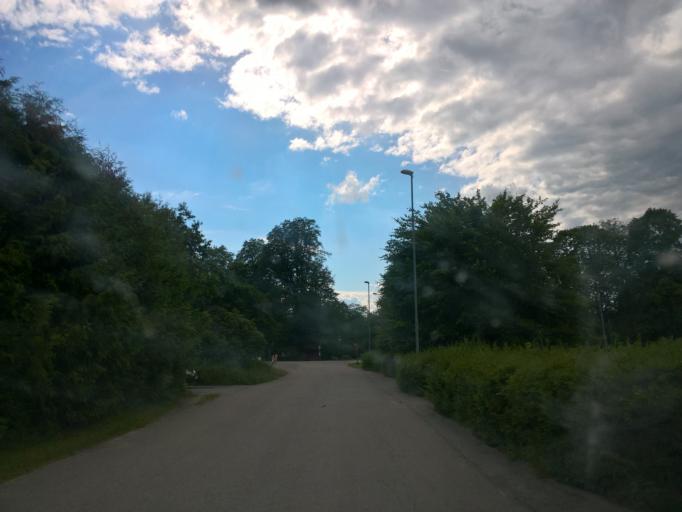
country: SE
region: OEstergoetland
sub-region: Finspangs Kommun
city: Finspang
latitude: 58.7364
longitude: 15.8285
